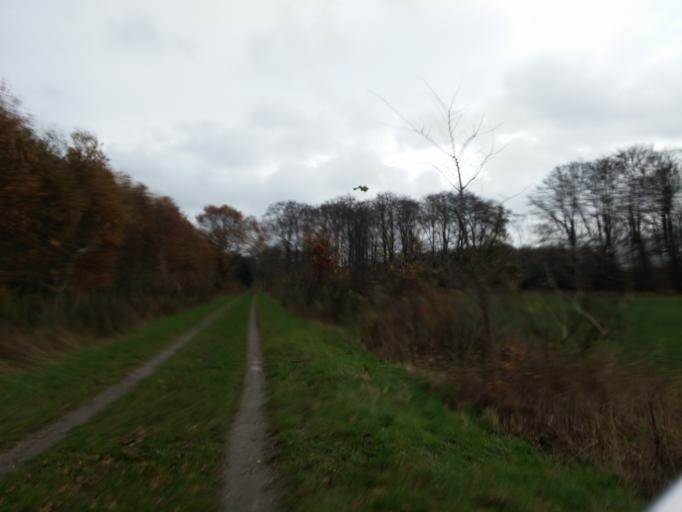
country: DK
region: South Denmark
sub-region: Kerteminde Kommune
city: Munkebo
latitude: 55.4296
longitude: 10.5462
